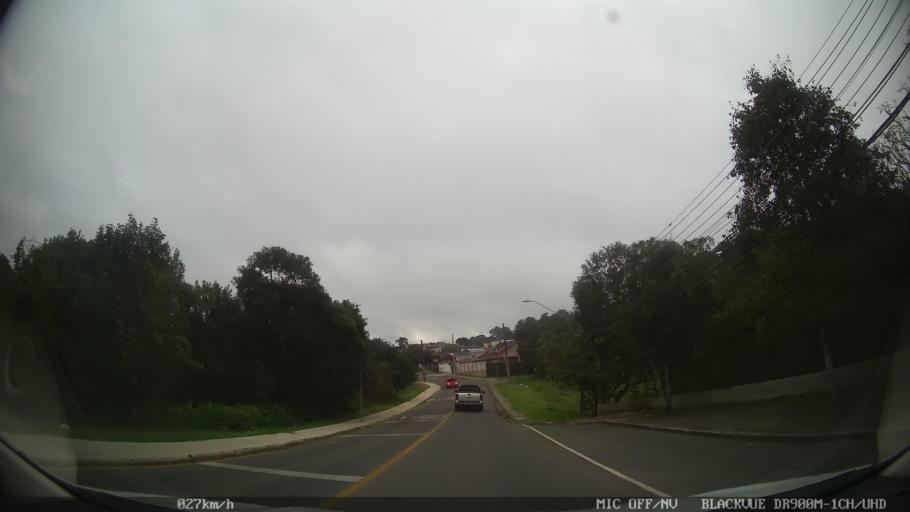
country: BR
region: Parana
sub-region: Almirante Tamandare
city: Almirante Tamandare
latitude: -25.3753
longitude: -49.3275
